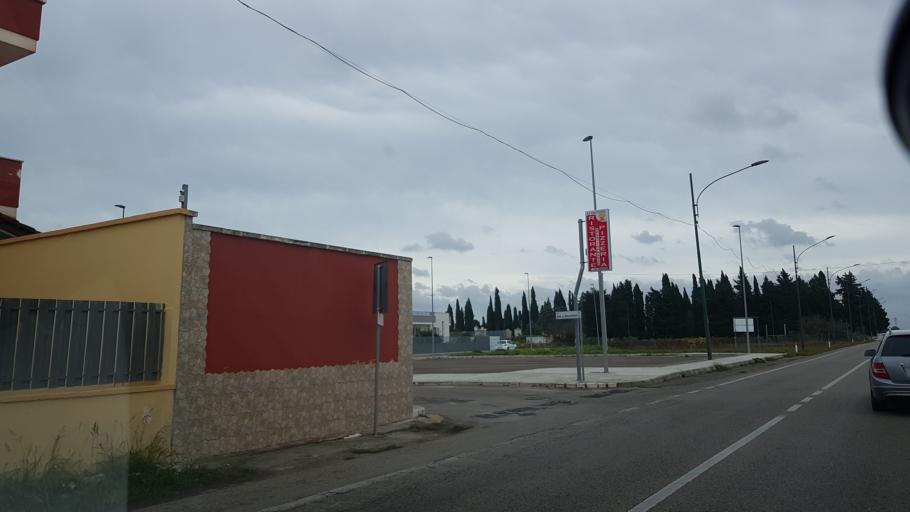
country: IT
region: Apulia
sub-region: Provincia di Lecce
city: Guagnano
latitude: 40.4011
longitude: 17.9569
